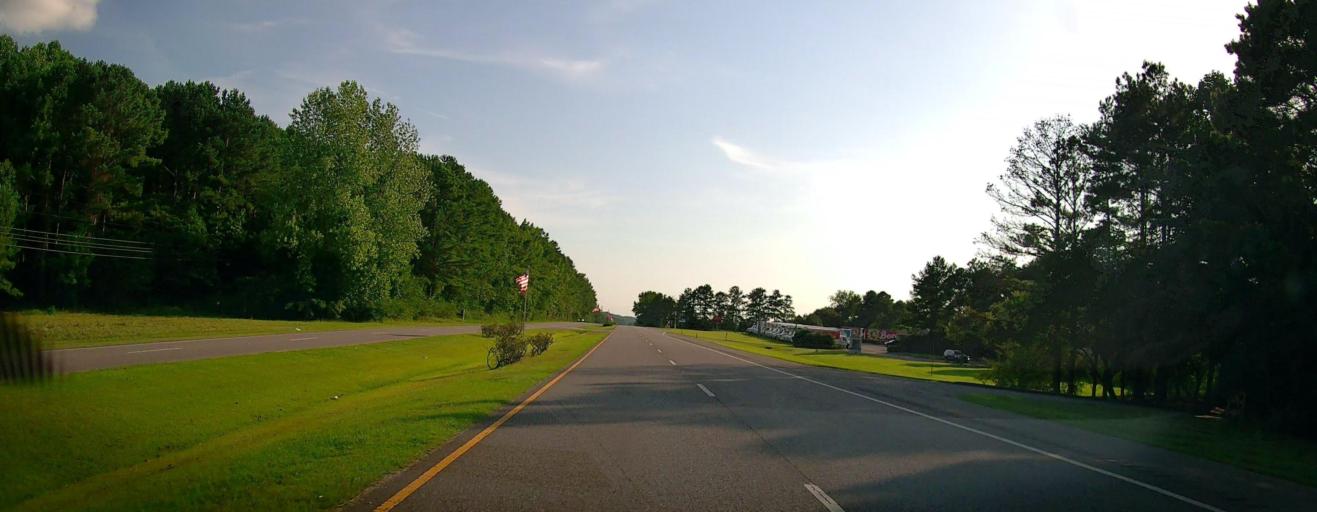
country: US
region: Alabama
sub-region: Jefferson County
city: Irondale
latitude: 33.5453
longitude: -86.6848
